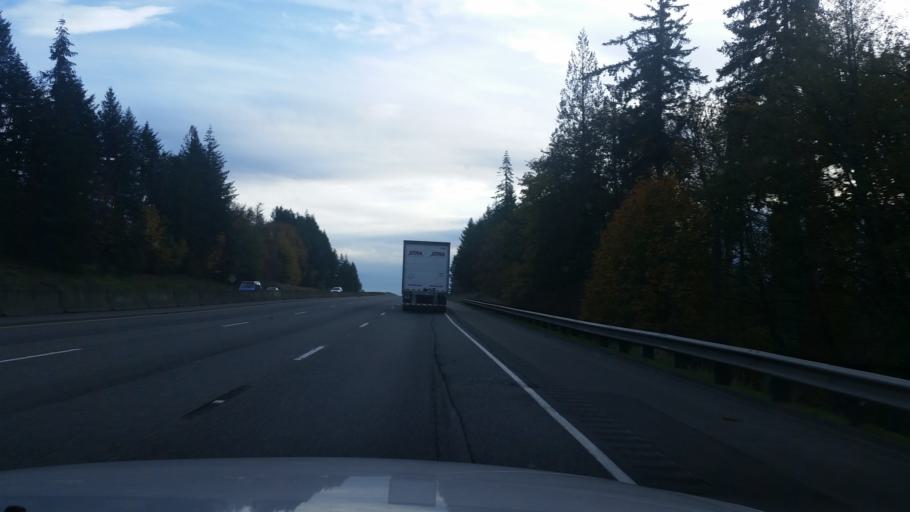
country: US
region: Washington
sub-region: Thurston County
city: Tumwater
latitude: 46.9051
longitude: -122.9567
